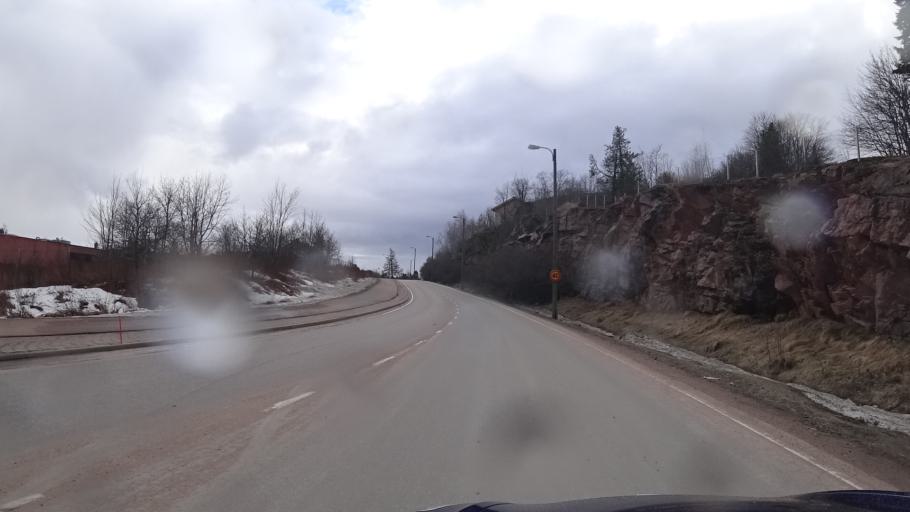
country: FI
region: Kymenlaakso
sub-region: Kotka-Hamina
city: Karhula
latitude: 60.5341
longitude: 26.9085
